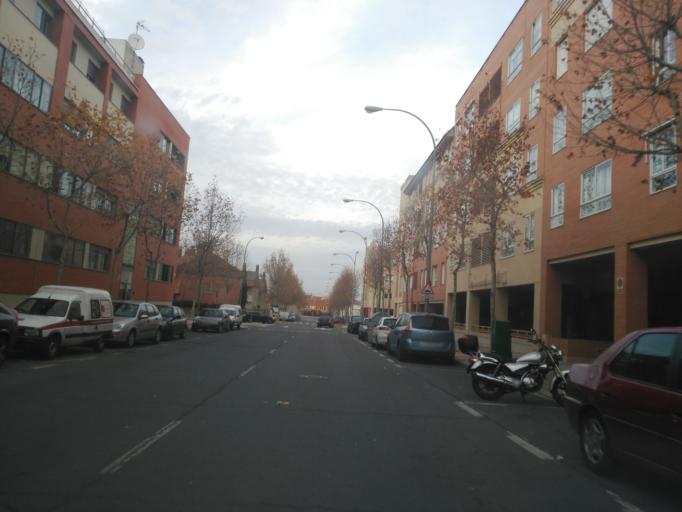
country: ES
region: Castille and Leon
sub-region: Provincia de Salamanca
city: Salamanca
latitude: 40.9472
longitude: -5.6721
